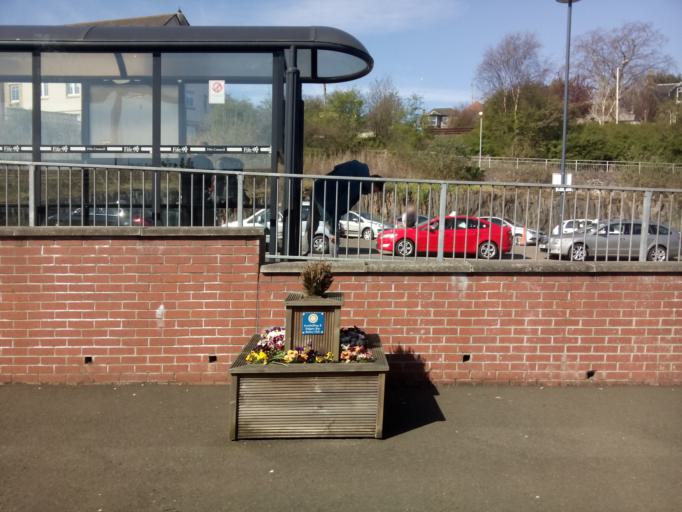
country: GB
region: Scotland
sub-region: Fife
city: Inverkeithing
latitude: 56.0346
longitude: -3.3954
